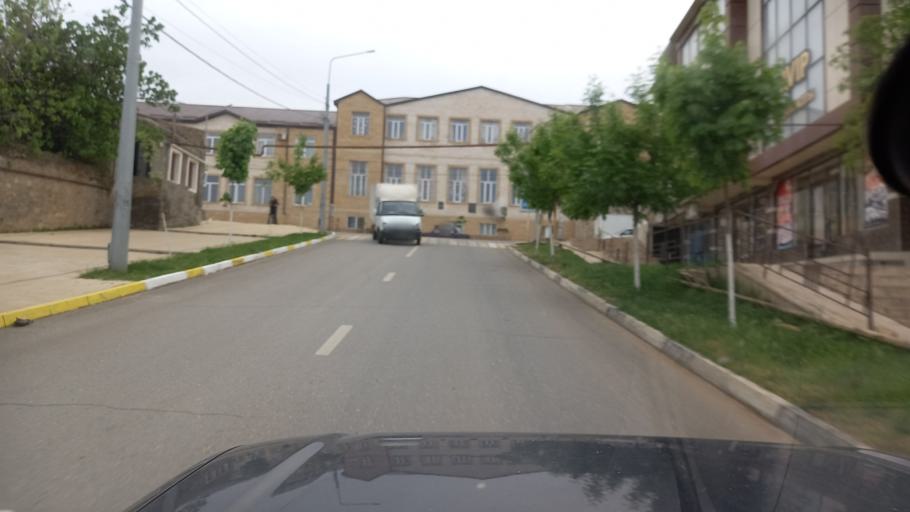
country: RU
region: Dagestan
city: Derbent
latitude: 42.0542
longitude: 48.2835
